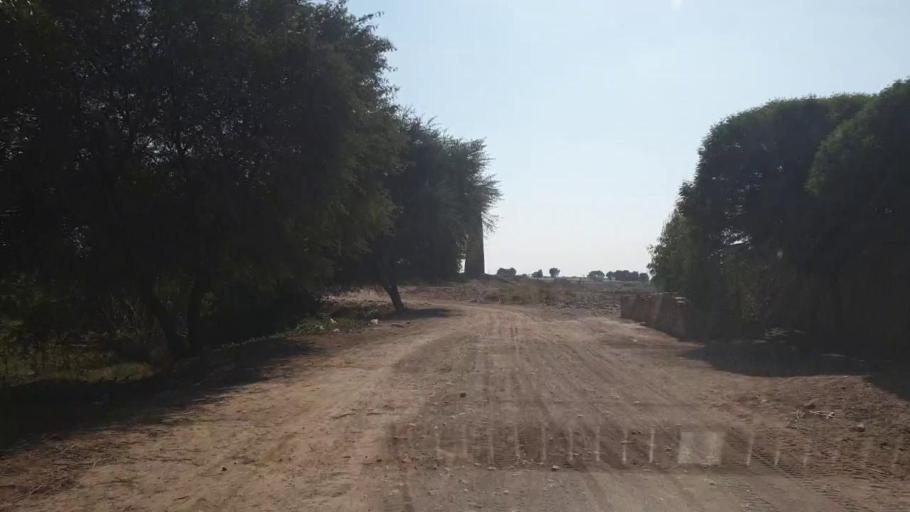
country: PK
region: Sindh
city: Tando Allahyar
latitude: 25.4275
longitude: 68.6938
